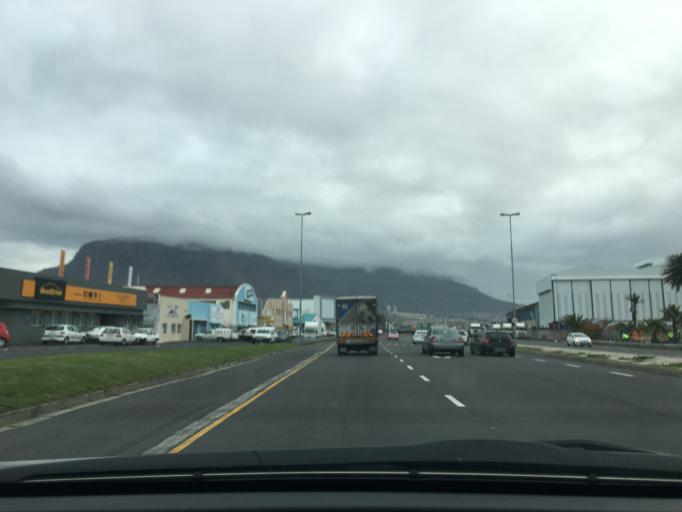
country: ZA
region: Western Cape
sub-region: City of Cape Town
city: Rosebank
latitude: -33.9145
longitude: 18.4655
